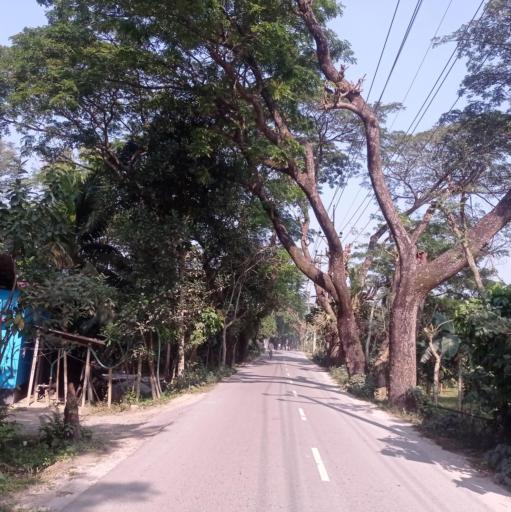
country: BD
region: Dhaka
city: Narsingdi
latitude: 24.0499
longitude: 90.6817
